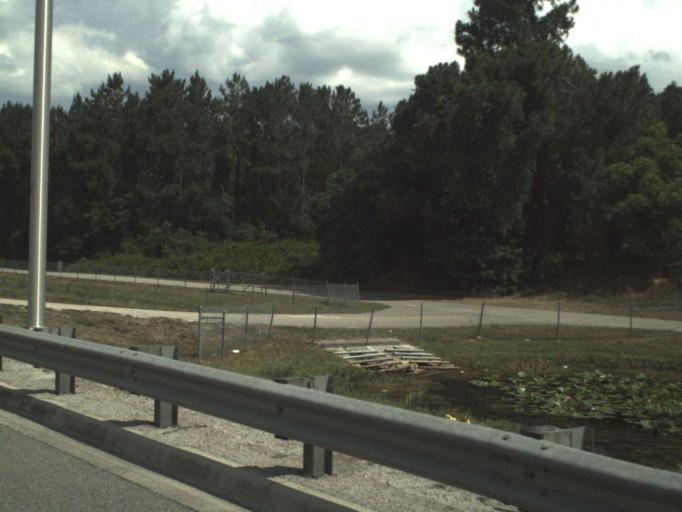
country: US
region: Florida
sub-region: Lake County
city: Silver Lake
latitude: 28.8179
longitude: -81.7703
